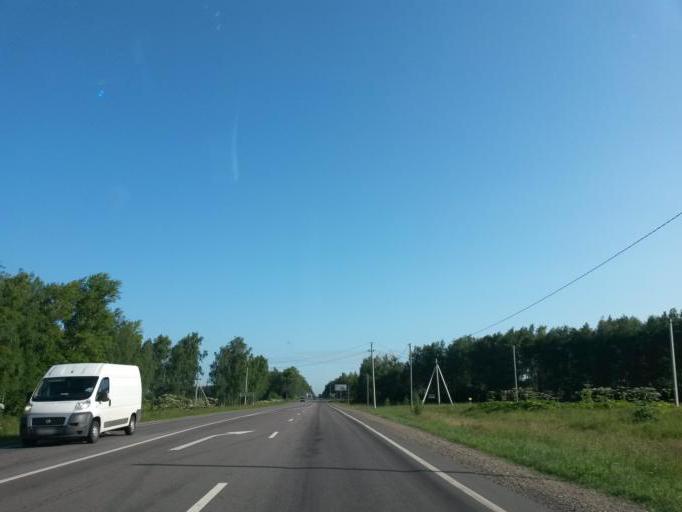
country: RU
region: Moskovskaya
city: Belyye Stolby
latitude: 55.2739
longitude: 37.8262
